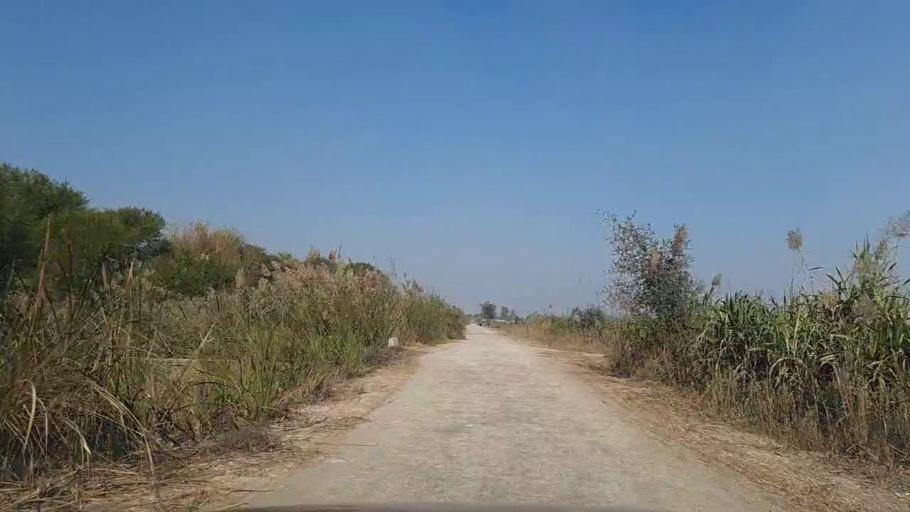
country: PK
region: Sindh
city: Daur
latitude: 26.5029
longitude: 68.3463
